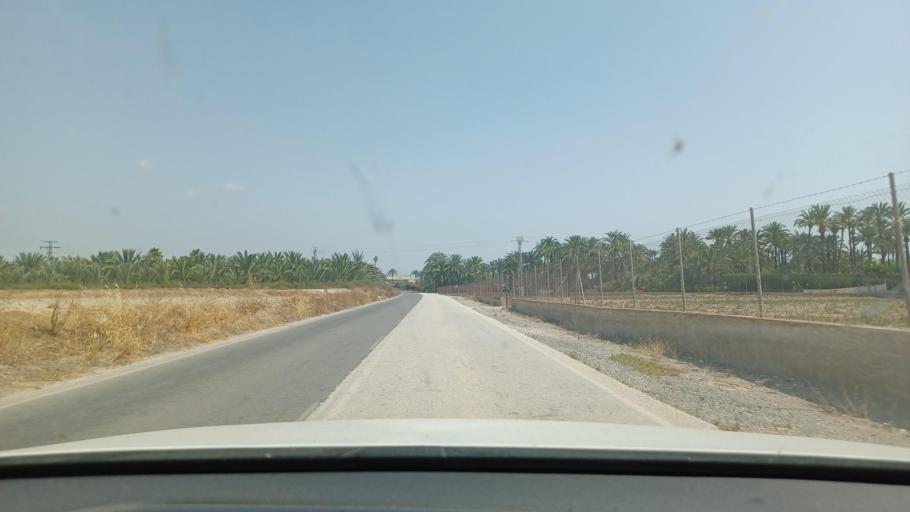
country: ES
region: Valencia
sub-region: Provincia de Alicante
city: Elche
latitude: 38.2453
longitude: -0.6911
